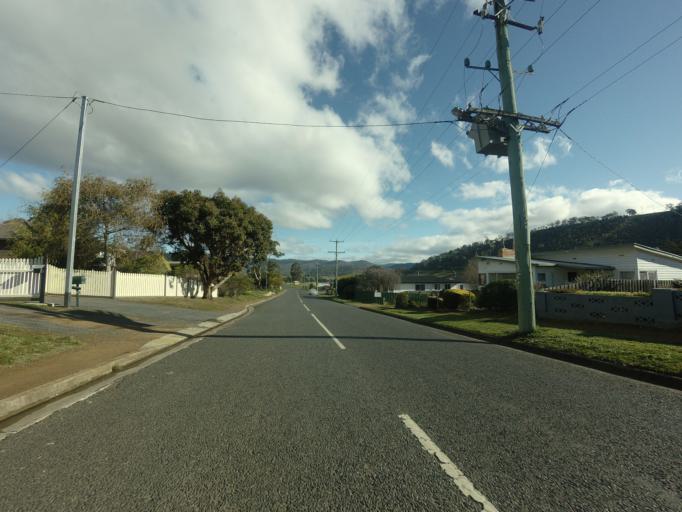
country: AU
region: Tasmania
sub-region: Derwent Valley
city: New Norfolk
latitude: -42.7568
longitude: 147.0502
